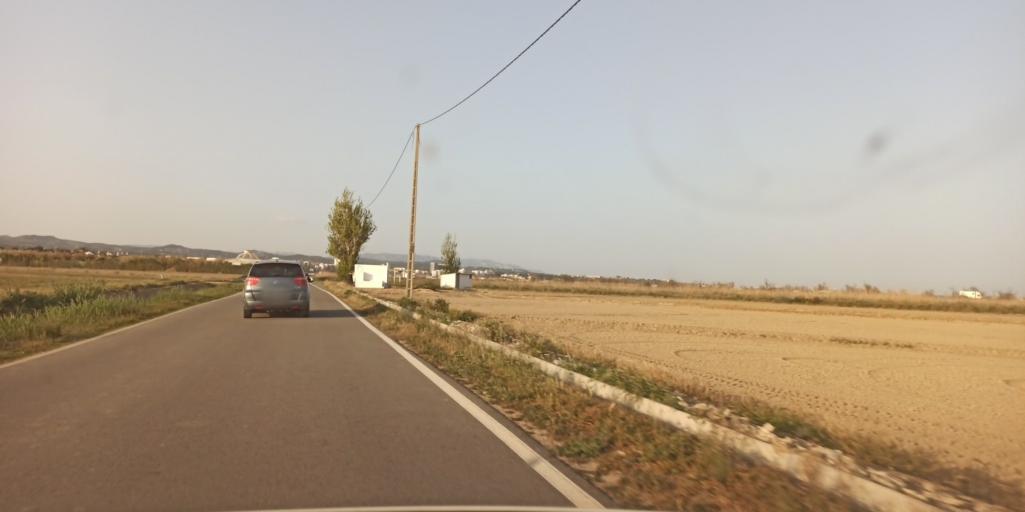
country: ES
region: Catalonia
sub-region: Provincia de Tarragona
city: L'Ampolla
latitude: 40.7940
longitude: 0.6991
